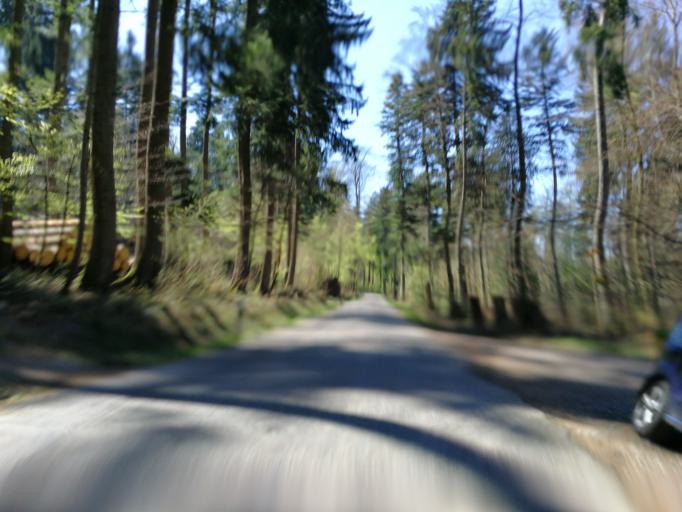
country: CH
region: Zurich
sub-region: Bezirk Uster
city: Aesch
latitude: 47.3077
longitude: 8.6545
